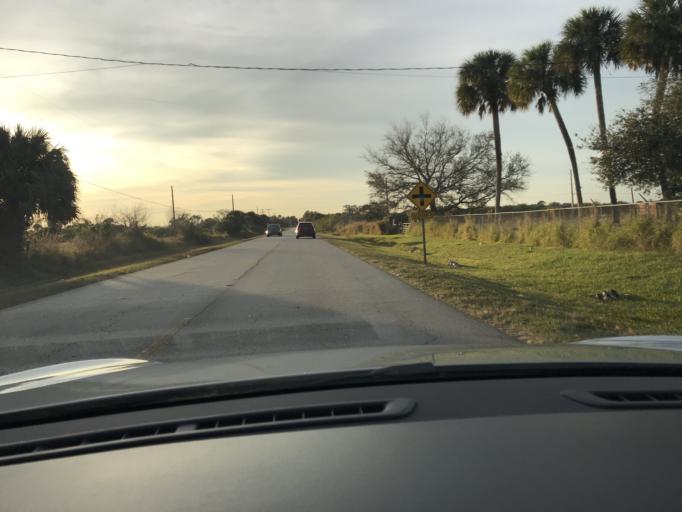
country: US
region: Florida
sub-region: Saint Lucie County
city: Lakewood Park
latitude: 27.4842
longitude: -80.3880
